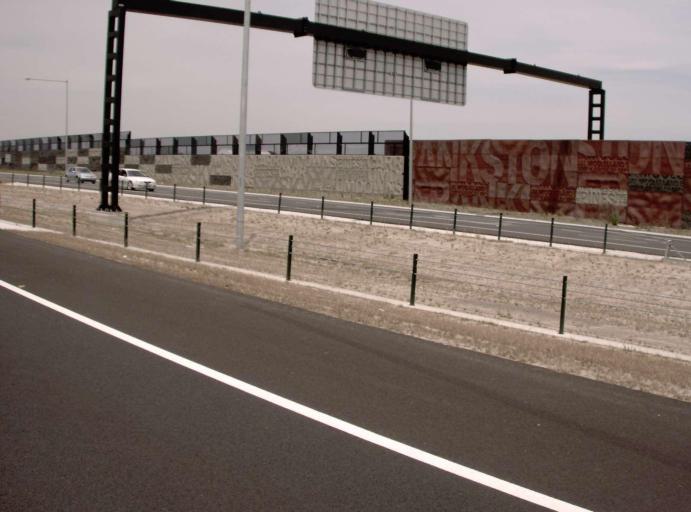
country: AU
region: Victoria
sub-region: Frankston
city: Carrum Downs
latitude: -38.1028
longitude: 145.1583
